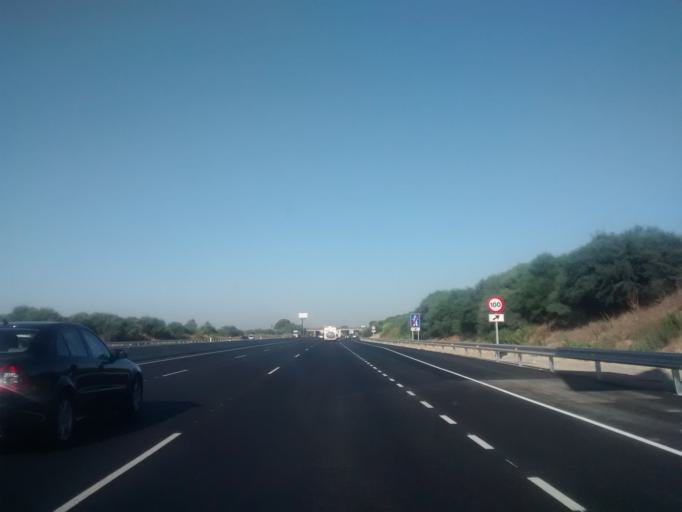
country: ES
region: Andalusia
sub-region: Provincia de Sevilla
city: Bollullos de la Mitacion
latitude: 37.3615
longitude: -6.1360
